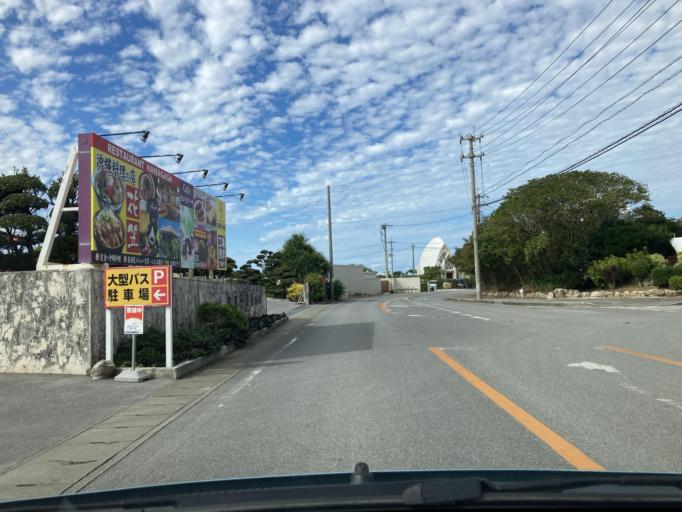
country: JP
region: Okinawa
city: Ishikawa
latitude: 26.4332
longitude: 127.7190
